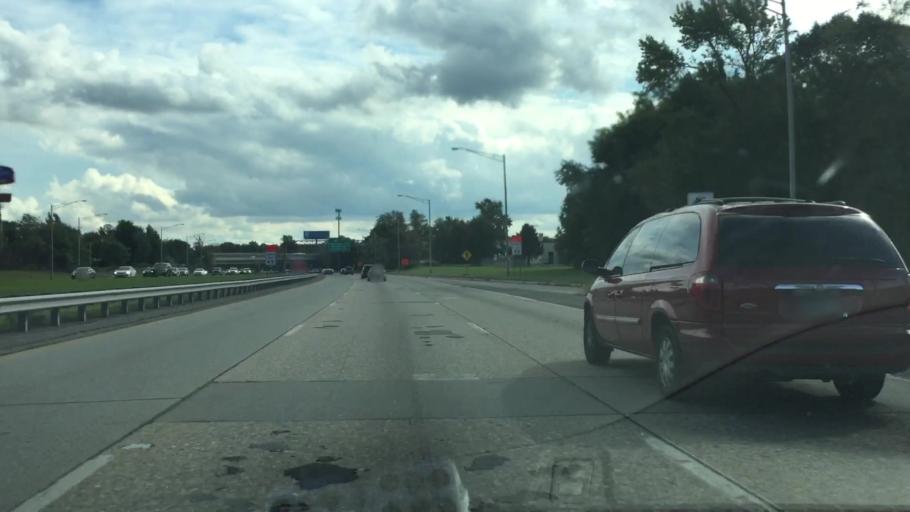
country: US
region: New Jersey
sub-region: Camden County
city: Glendora
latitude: 39.8349
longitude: -75.0913
